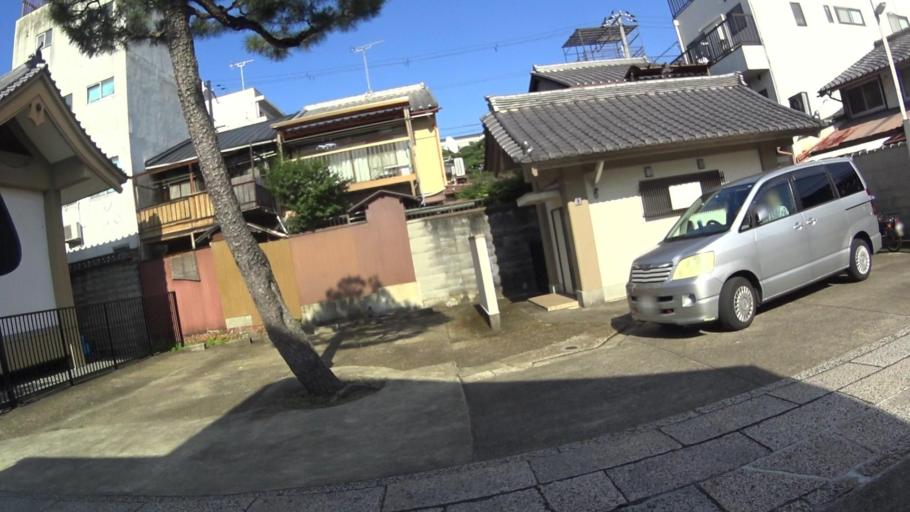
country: RU
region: Rostov
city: Remontnoye
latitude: 46.5011
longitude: 43.7609
